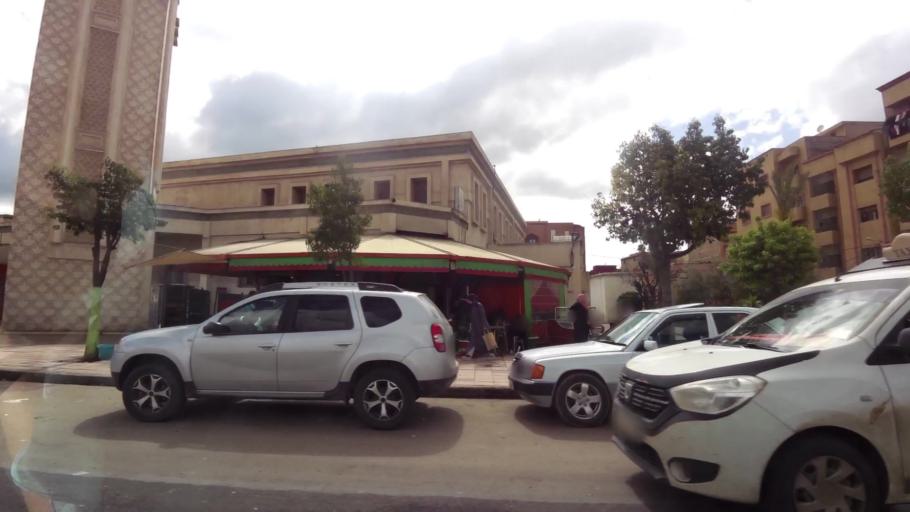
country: MA
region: Chaouia-Ouardigha
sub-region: Settat Province
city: Berrechid
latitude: 33.2709
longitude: -7.5859
